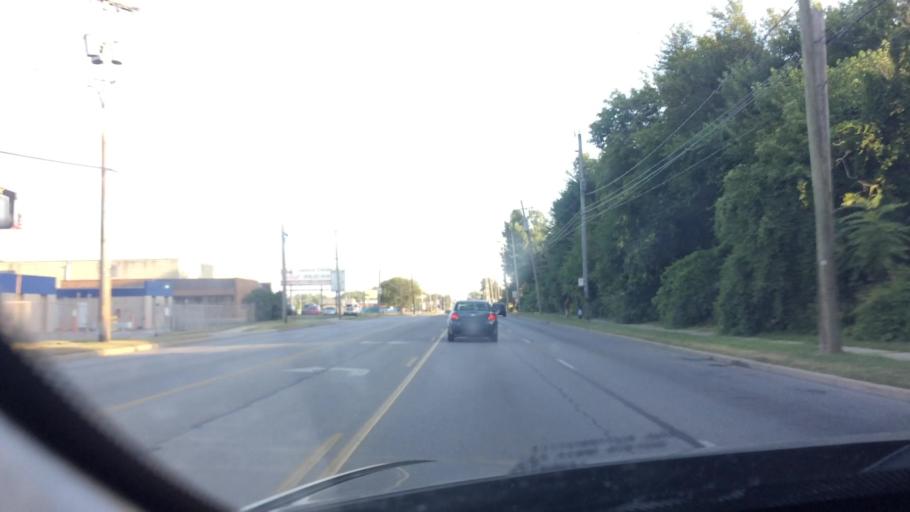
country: US
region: Ohio
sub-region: Lucas County
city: Ottawa Hills
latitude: 41.6423
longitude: -83.6260
